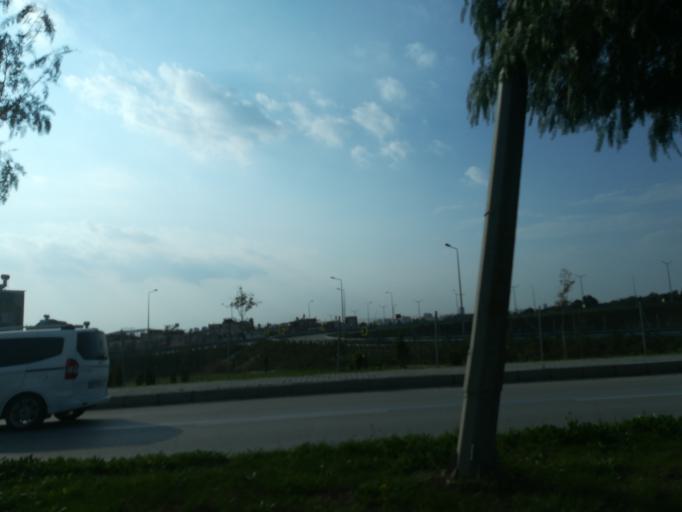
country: TR
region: Adana
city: Adana
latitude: 37.0218
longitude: 35.3427
